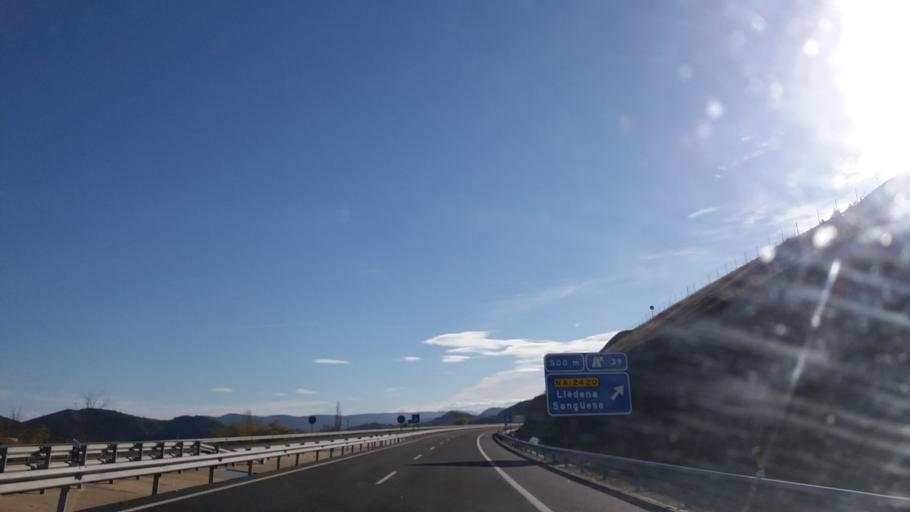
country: ES
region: Navarre
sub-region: Provincia de Navarra
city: Lumbier
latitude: 42.6250
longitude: -1.3100
